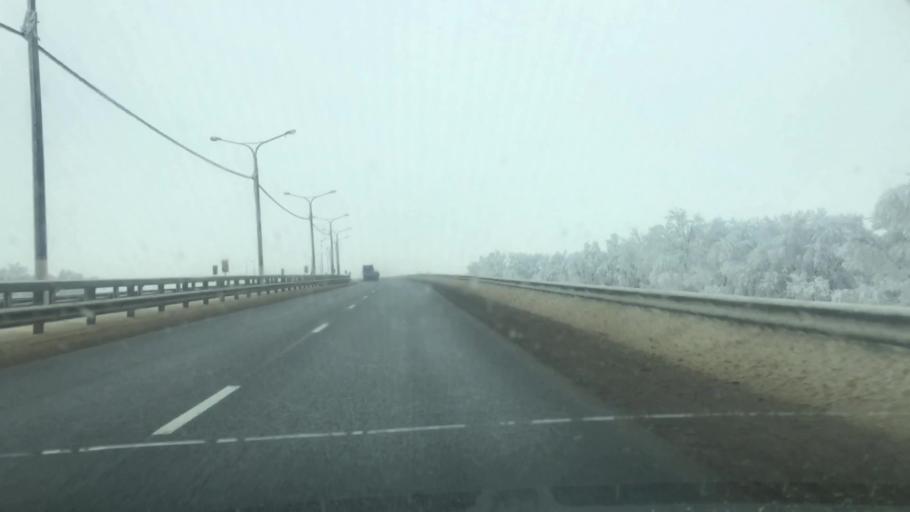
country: RU
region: Lipetsk
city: Yelets
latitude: 52.5473
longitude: 38.7185
